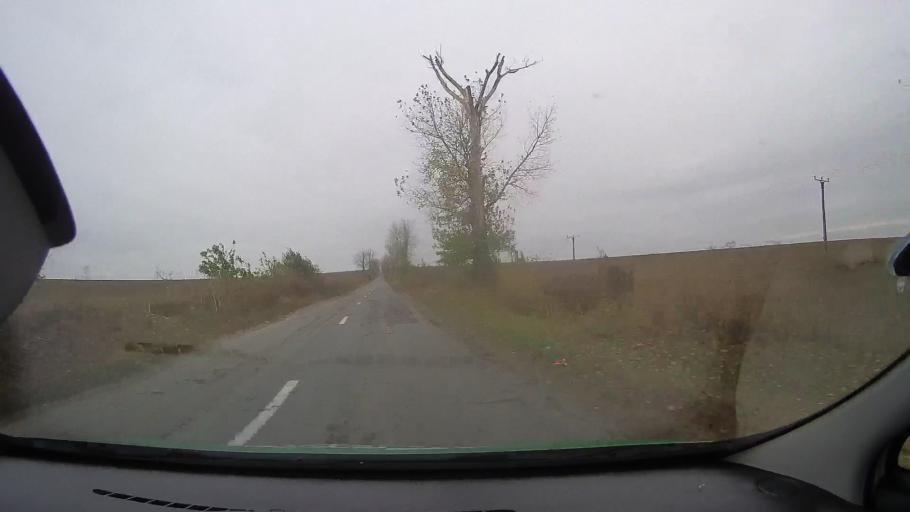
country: RO
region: Constanta
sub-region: Comuna Pantelimon
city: Pantelimon
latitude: 44.5544
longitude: 28.3260
